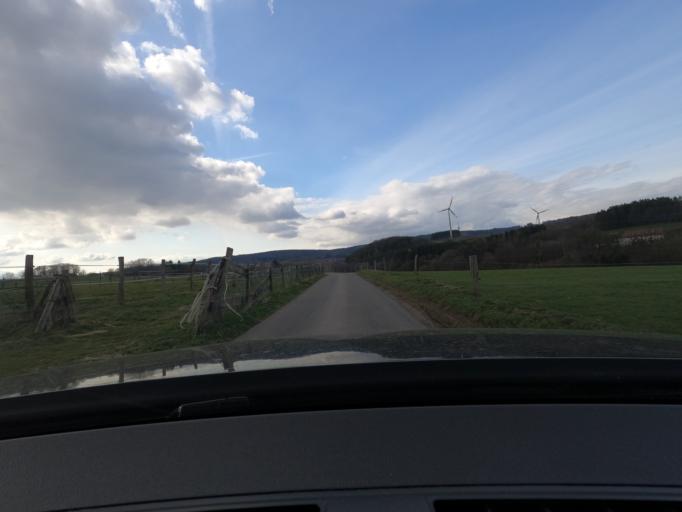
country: DE
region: North Rhine-Westphalia
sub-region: Regierungsbezirk Arnsberg
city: Herscheid
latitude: 51.1124
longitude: 7.7831
